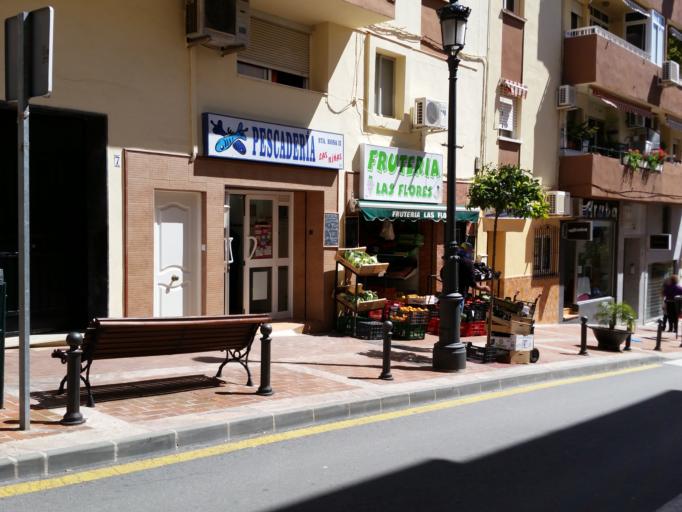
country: ES
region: Andalusia
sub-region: Provincia de Malaga
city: Benalmadena
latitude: 36.6021
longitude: -4.5342
